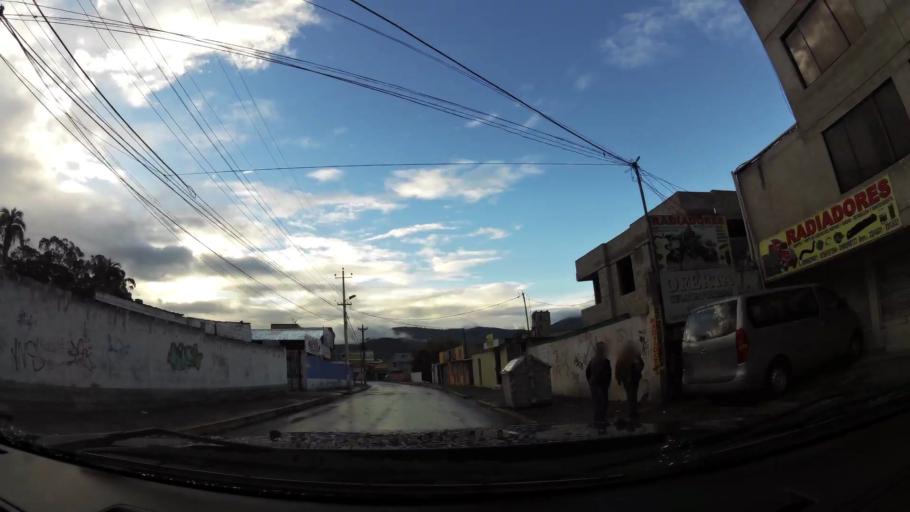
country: EC
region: Pichincha
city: Quito
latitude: -0.1128
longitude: -78.4997
